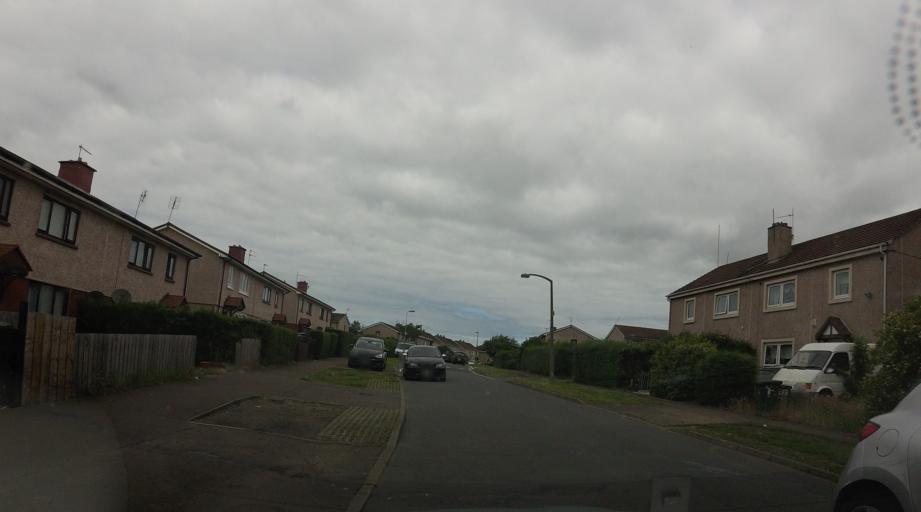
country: GB
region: Scotland
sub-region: Midlothian
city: Loanhead
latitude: 55.8965
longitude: -3.1585
